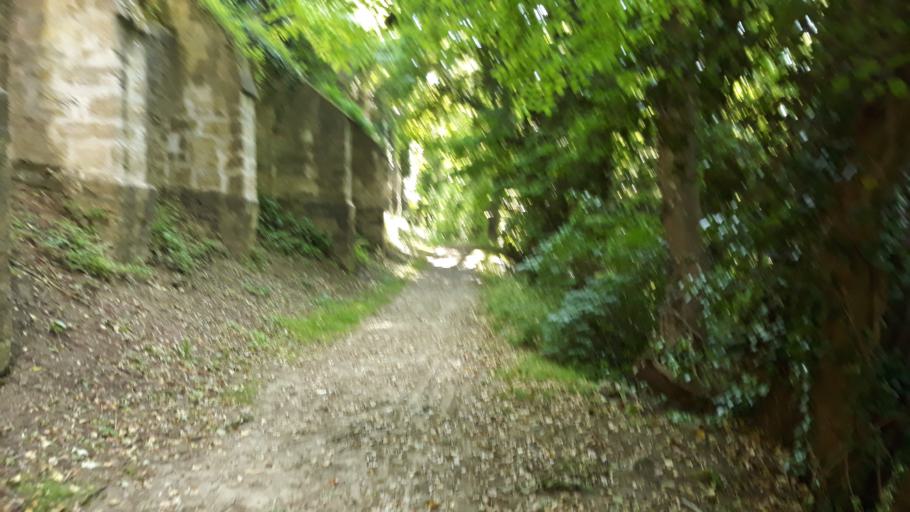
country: FR
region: Picardie
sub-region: Departement de l'Aisne
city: Laon
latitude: 49.5573
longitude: 3.6167
